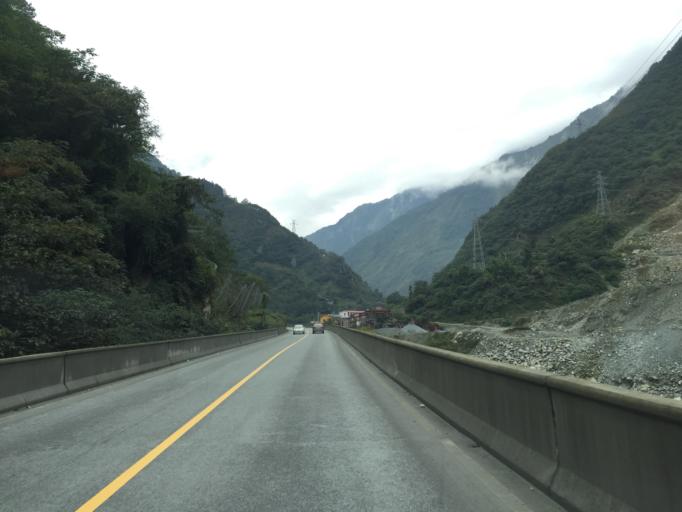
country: CN
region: Sichuan
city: Guangsheng
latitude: 31.0686
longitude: 103.4732
